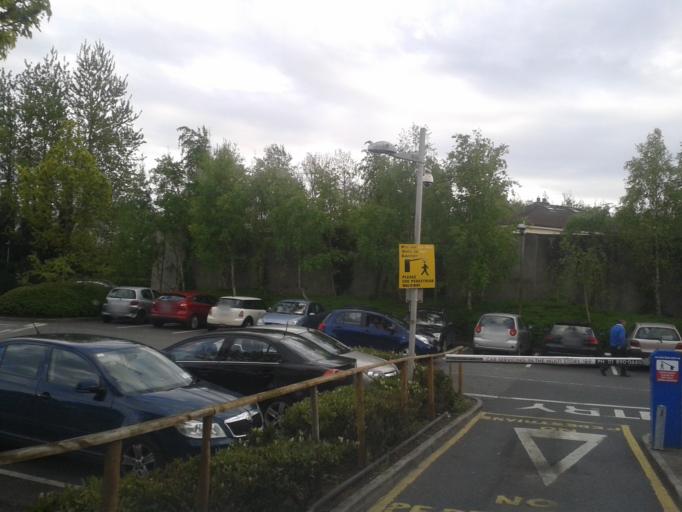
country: IE
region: Leinster
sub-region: Fingal County
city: Swords
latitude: 53.4527
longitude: -6.2193
